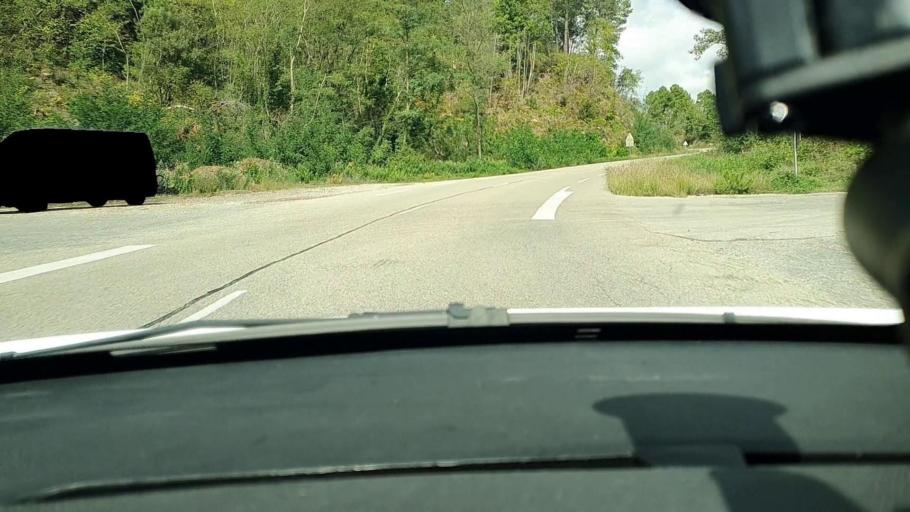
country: FR
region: Languedoc-Roussillon
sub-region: Departement du Gard
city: Laval-Pradel
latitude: 44.2290
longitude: 4.0534
